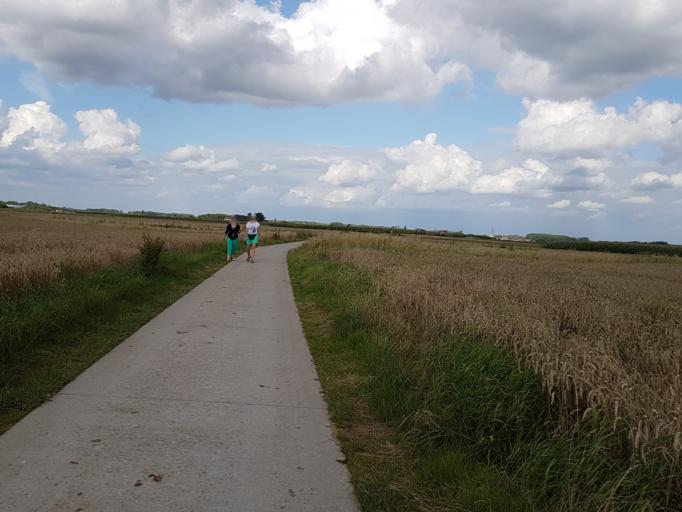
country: BE
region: Flanders
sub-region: Provincie Vlaams-Brabant
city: Kortenberg
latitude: 50.9117
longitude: 4.5378
